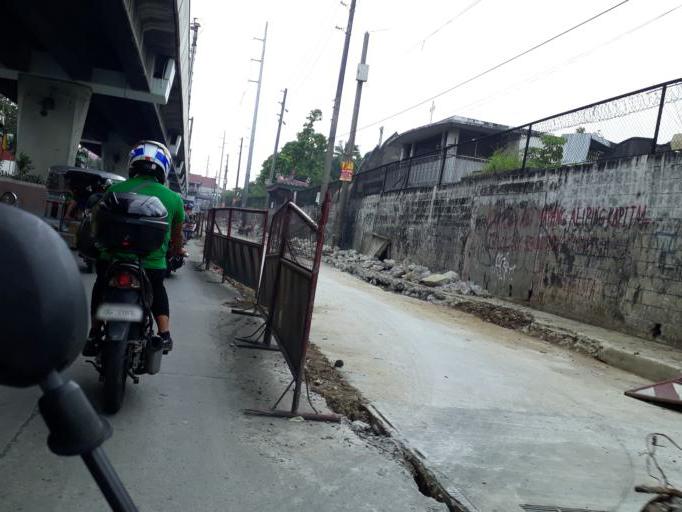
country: PH
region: Metro Manila
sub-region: City of Manila
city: Manila
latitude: 14.6336
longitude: 120.9814
